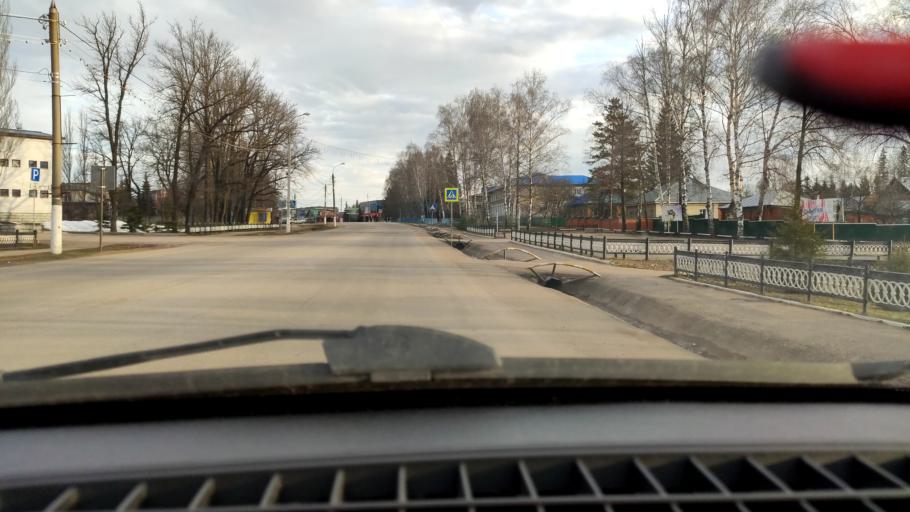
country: RU
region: Bashkortostan
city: Tolbazy
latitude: 54.0132
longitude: 55.8863
